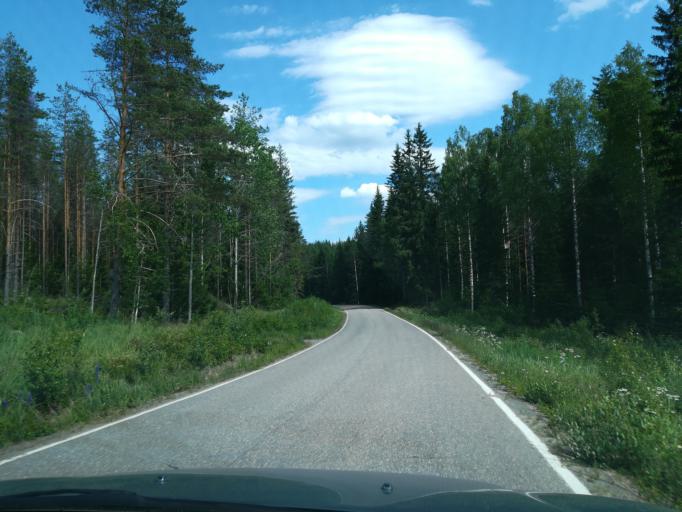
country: FI
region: South Karelia
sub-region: Imatra
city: Ruokolahti
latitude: 61.4742
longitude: 28.7940
